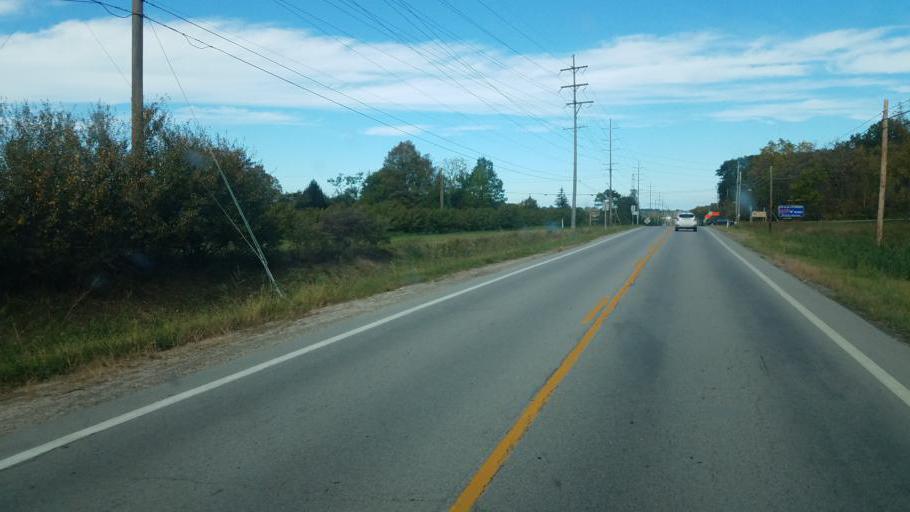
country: US
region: Ohio
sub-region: Erie County
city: Huron
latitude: 41.3303
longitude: -82.4935
